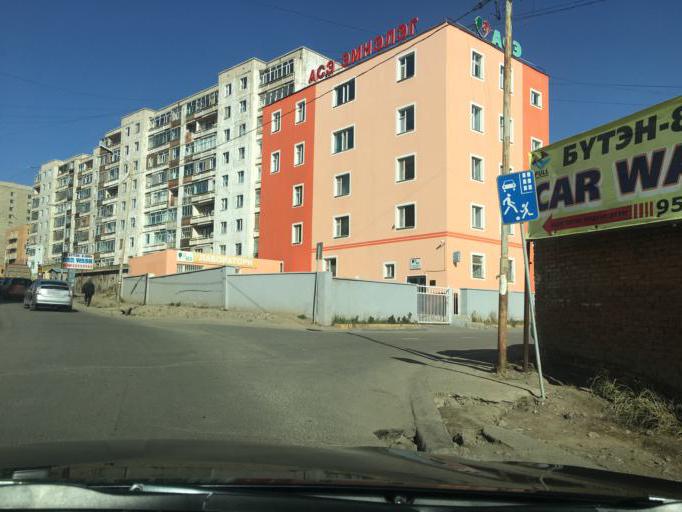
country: MN
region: Ulaanbaatar
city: Ulaanbaatar
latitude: 47.9259
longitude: 106.8766
